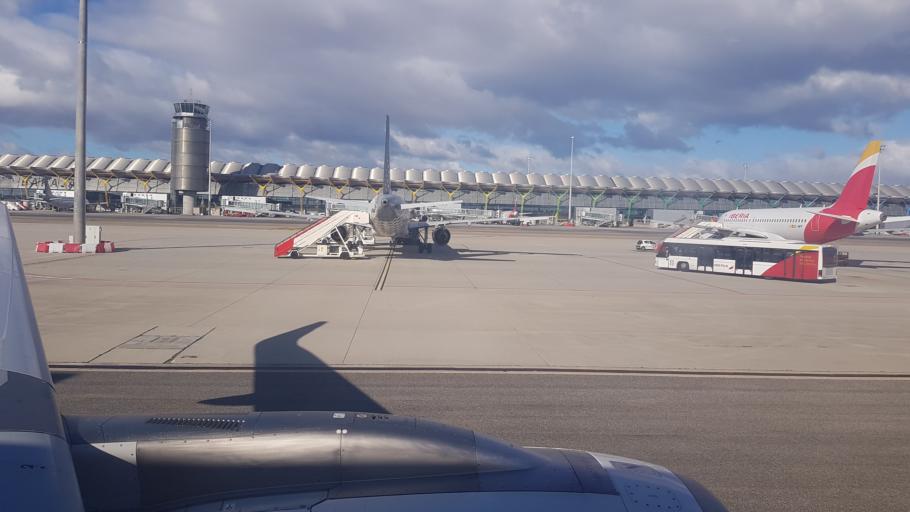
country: ES
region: Madrid
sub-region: Provincia de Madrid
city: Barajas de Madrid
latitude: 40.4931
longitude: -3.5865
